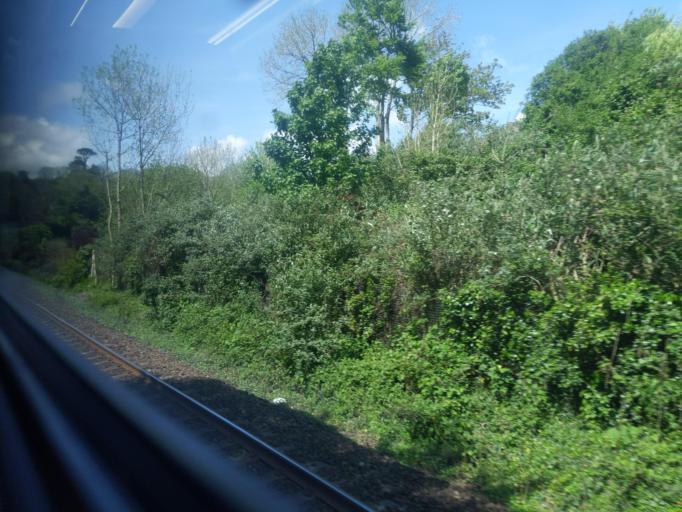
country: GB
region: England
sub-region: Cornwall
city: St Austell
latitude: 50.3417
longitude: -4.7962
